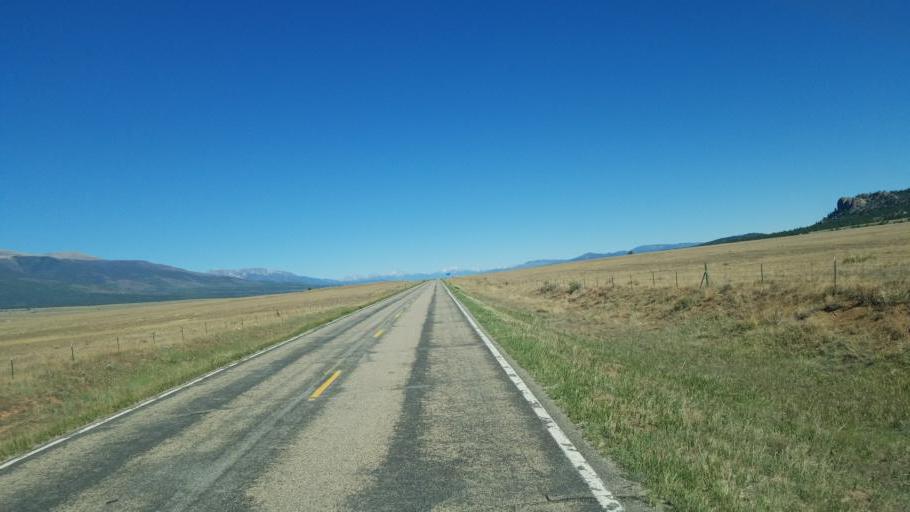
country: US
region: Colorado
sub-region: Custer County
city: Westcliffe
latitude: 38.1996
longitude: -105.5325
